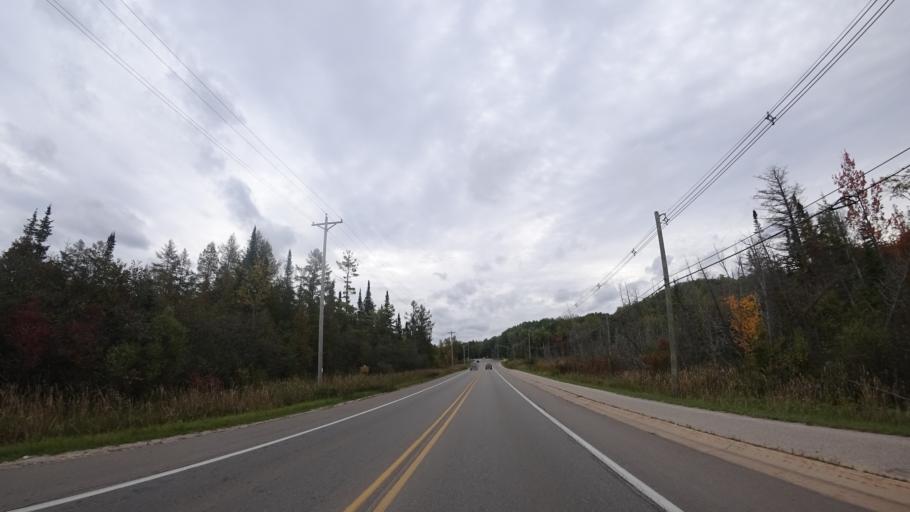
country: US
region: Michigan
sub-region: Emmet County
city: Petoskey
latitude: 45.4176
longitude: -84.9045
